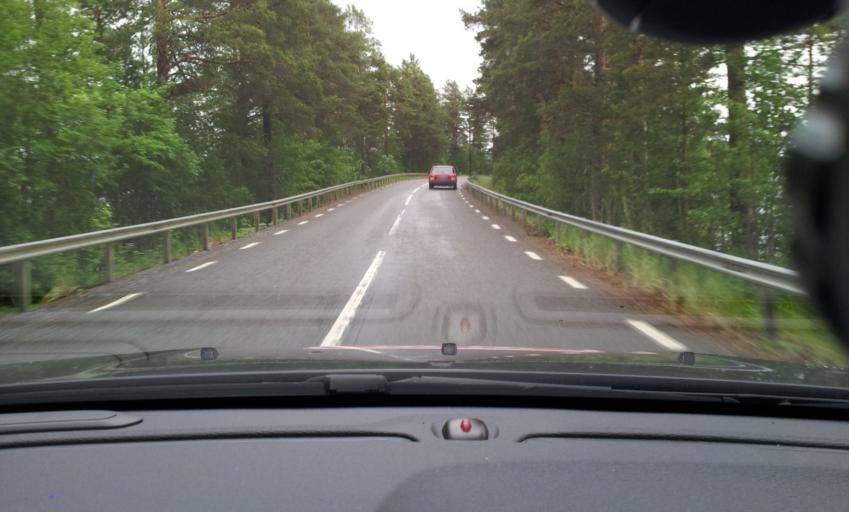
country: SE
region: Jaemtland
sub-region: Stroemsunds Kommun
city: Stroemsund
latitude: 63.5152
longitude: 15.4573
